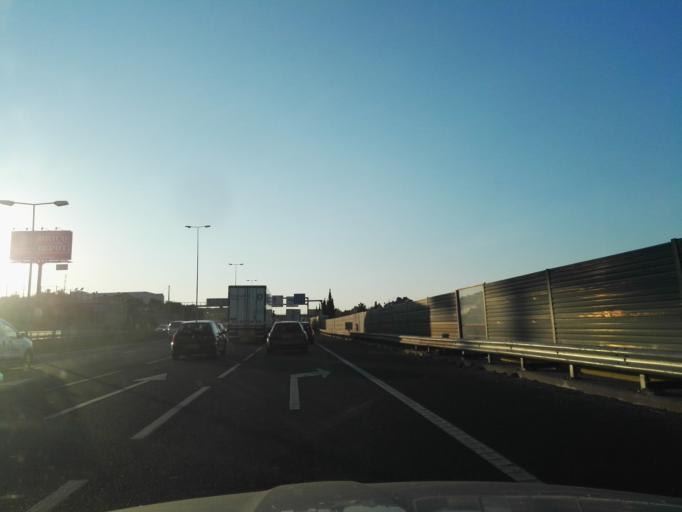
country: PT
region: Lisbon
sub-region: Loures
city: Camarate
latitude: 38.8001
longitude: -9.1279
